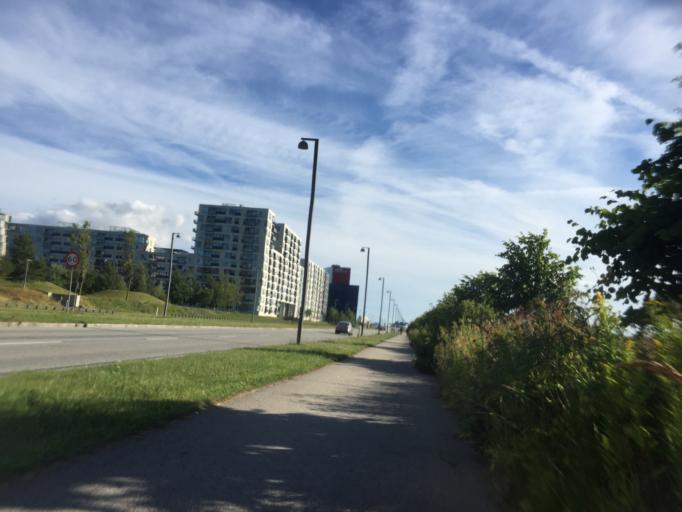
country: DK
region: Capital Region
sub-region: Tarnby Kommune
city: Tarnby
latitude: 55.6352
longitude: 12.5734
